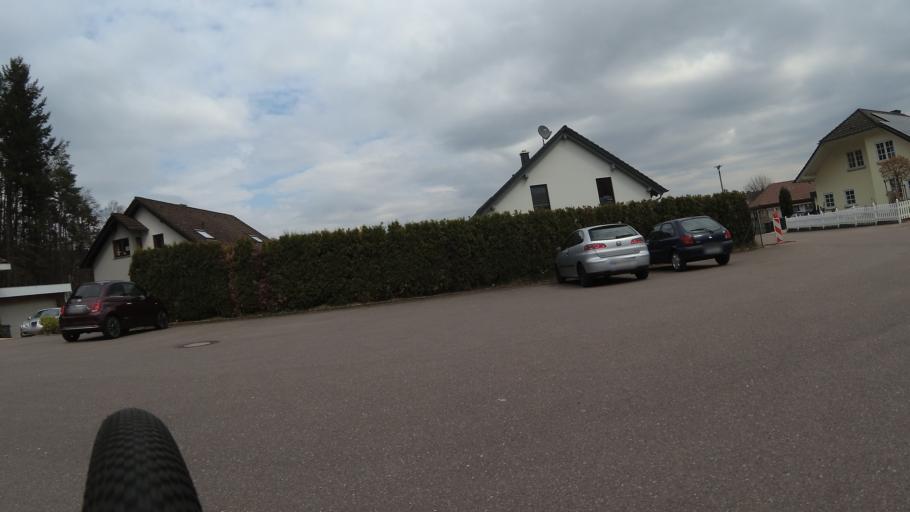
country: DE
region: Saarland
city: Mettlach
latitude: 49.4652
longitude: 6.5860
